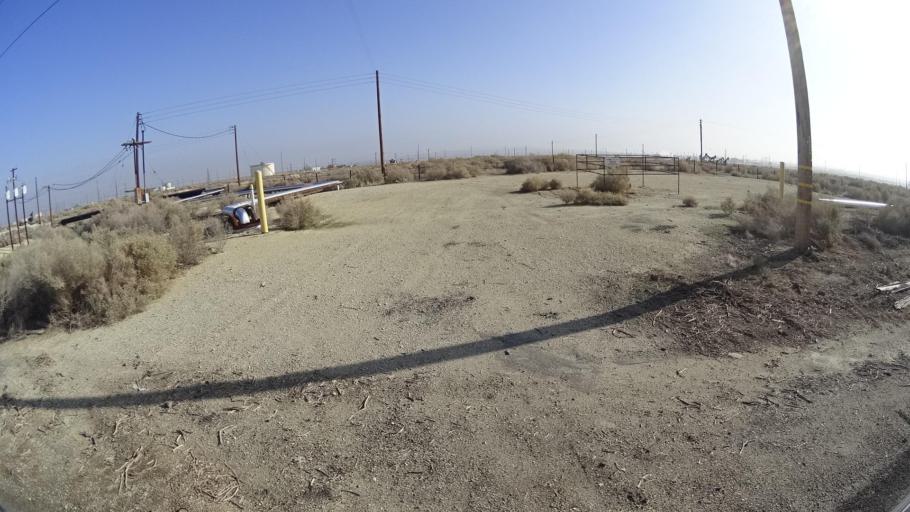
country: US
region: California
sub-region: Kern County
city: Taft Heights
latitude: 35.2144
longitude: -119.5697
